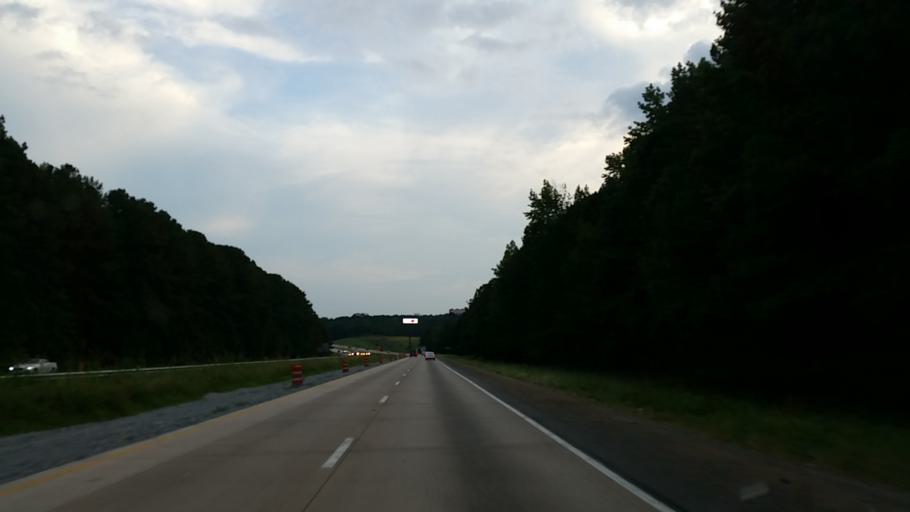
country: US
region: Georgia
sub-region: Forsyth County
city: Cumming
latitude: 34.1766
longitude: -84.1495
